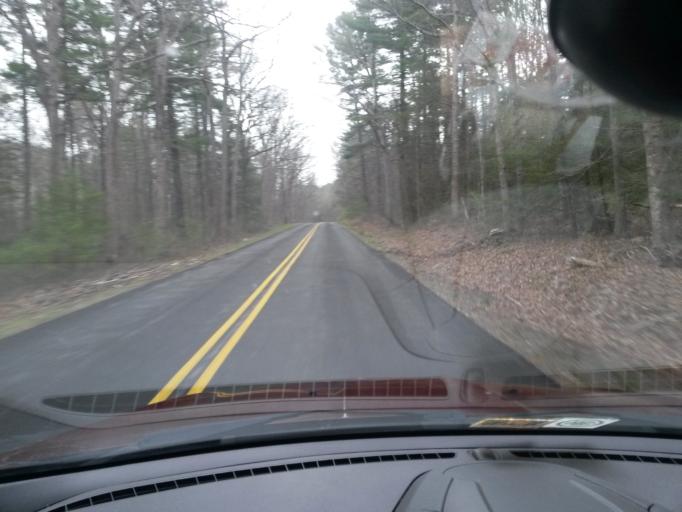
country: US
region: Virginia
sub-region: Alleghany County
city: Clifton Forge
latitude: 37.8184
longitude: -79.6696
